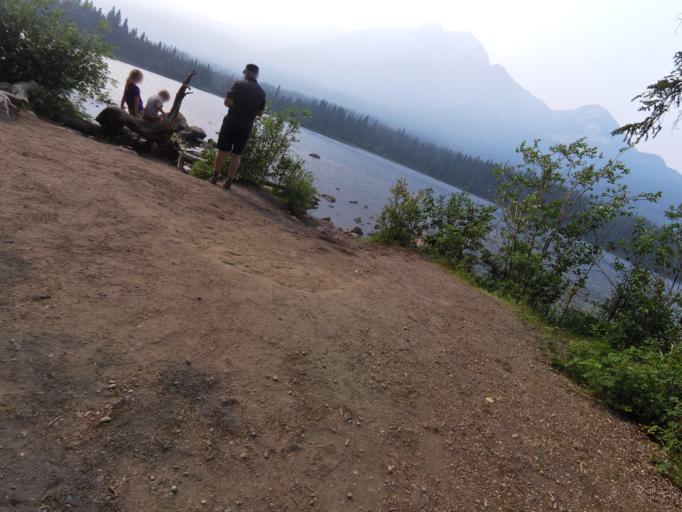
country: CA
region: Alberta
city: Jasper Park Lodge
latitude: 52.9256
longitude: -118.0988
